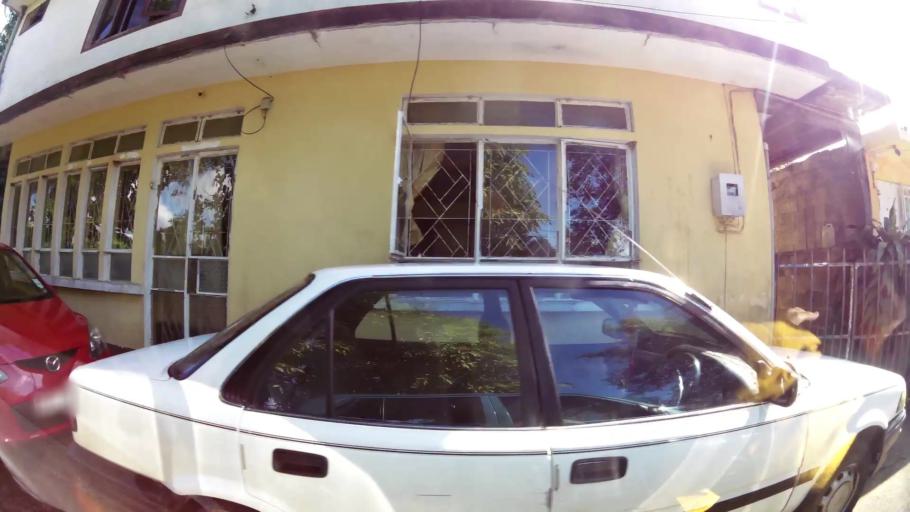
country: MU
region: Grand Port
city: Plaine Magnien
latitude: -20.4357
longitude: 57.6597
